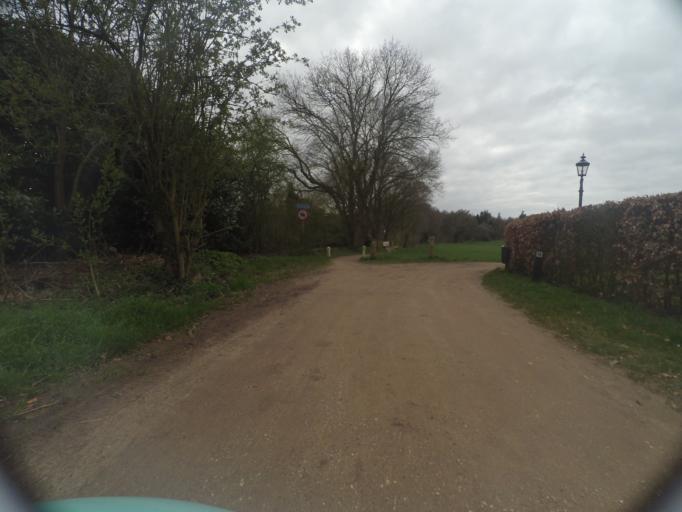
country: NL
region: Gelderland
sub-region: Gemeente Apeldoorn
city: Loenen
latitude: 52.1121
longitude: 6.0165
